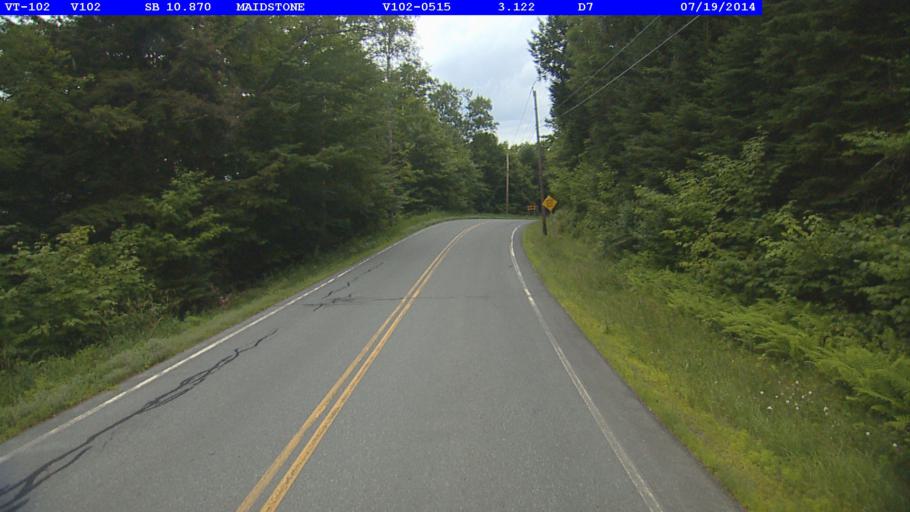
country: US
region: Vermont
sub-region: Essex County
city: Guildhall
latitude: 44.6073
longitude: -71.5607
